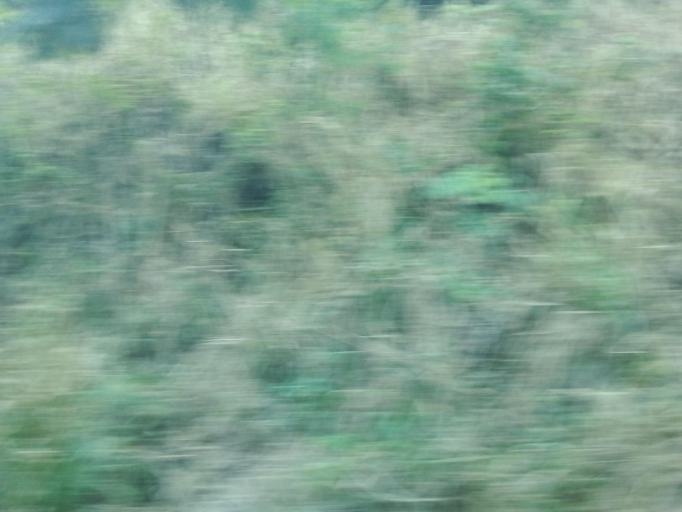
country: BR
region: Minas Gerais
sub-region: Ipaba
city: Ipaba
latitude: -19.4636
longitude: -42.4541
